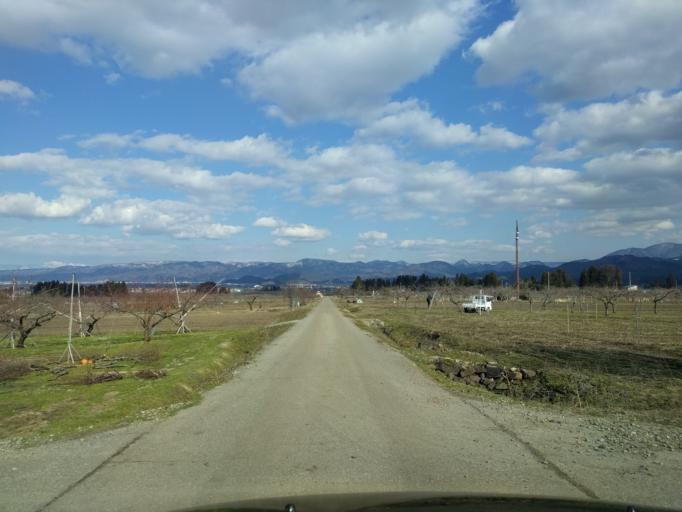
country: JP
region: Fukushima
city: Kitakata
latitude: 37.4475
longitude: 139.8103
